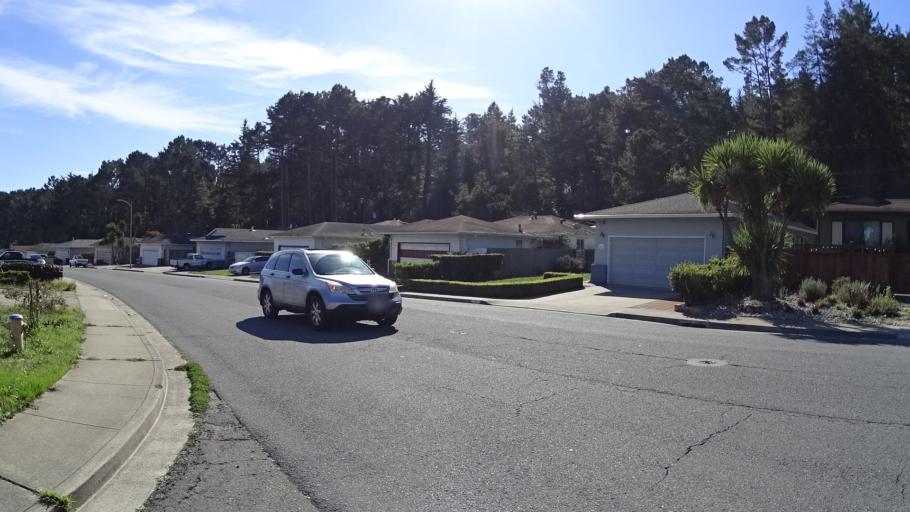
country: US
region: California
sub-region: San Mateo County
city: Pacifica
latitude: 37.6396
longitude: -122.4605
